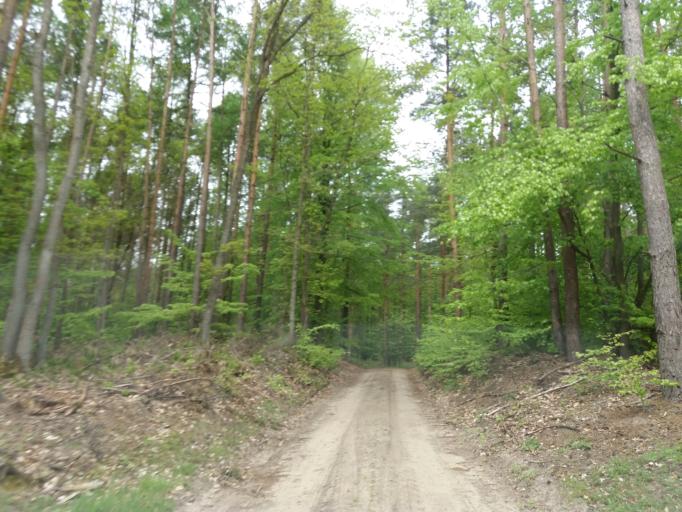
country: PL
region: West Pomeranian Voivodeship
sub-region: Powiat choszczenski
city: Bierzwnik
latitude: 53.0174
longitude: 15.6778
